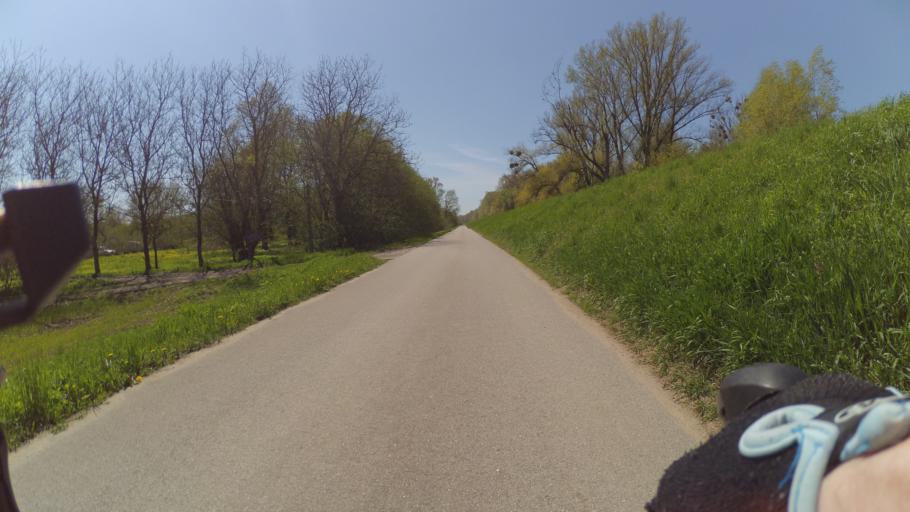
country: PL
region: Masovian Voivodeship
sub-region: Powiat plonski
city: Zaluski
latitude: 52.4033
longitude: 20.4654
